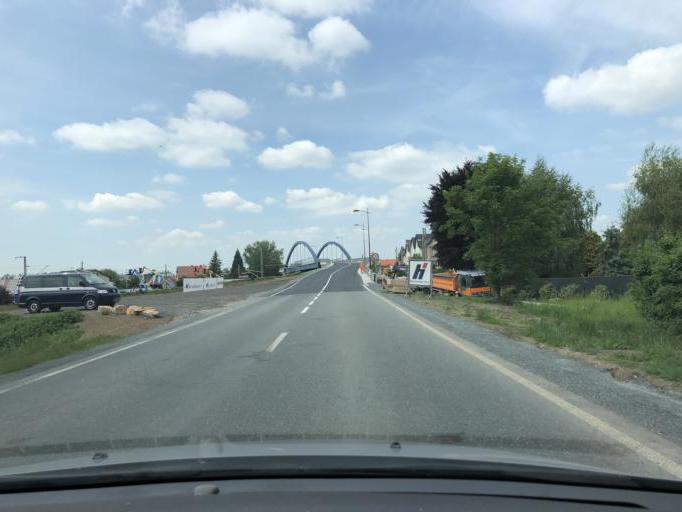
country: DE
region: Thuringia
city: Saara
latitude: 50.9334
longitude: 12.4291
